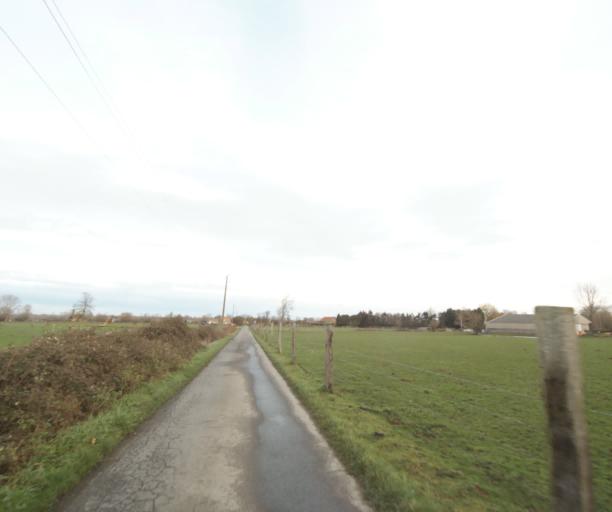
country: BE
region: Wallonia
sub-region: Province du Hainaut
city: Peruwelz
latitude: 50.4897
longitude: 3.5775
